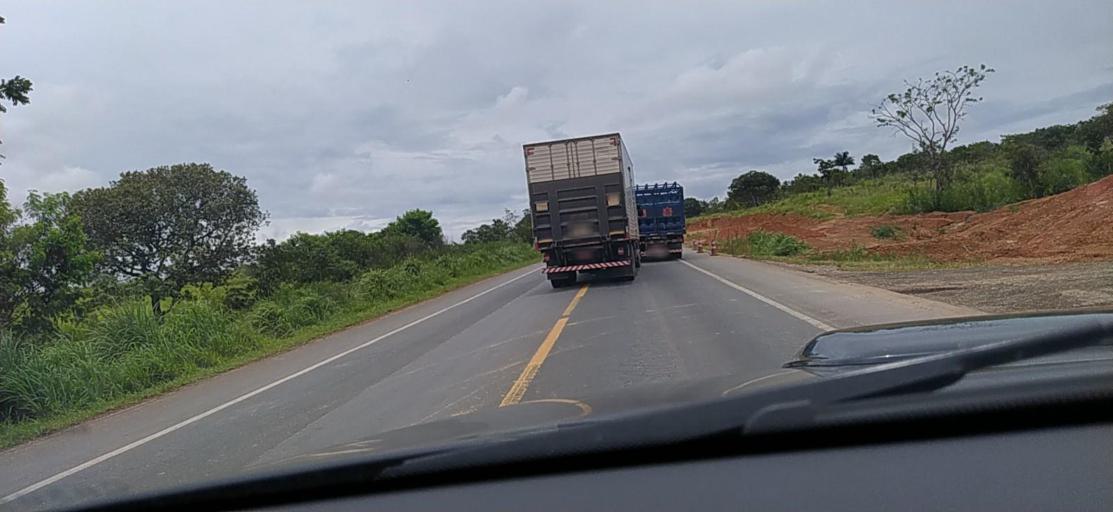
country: BR
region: Minas Gerais
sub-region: Curvelo
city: Curvelo
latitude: -18.7354
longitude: -44.4430
